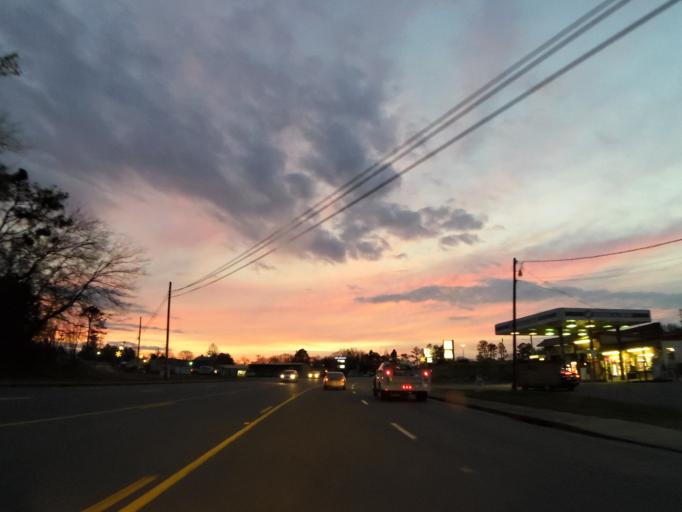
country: US
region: Tennessee
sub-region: Polk County
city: Benton
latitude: 35.1695
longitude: -84.6557
